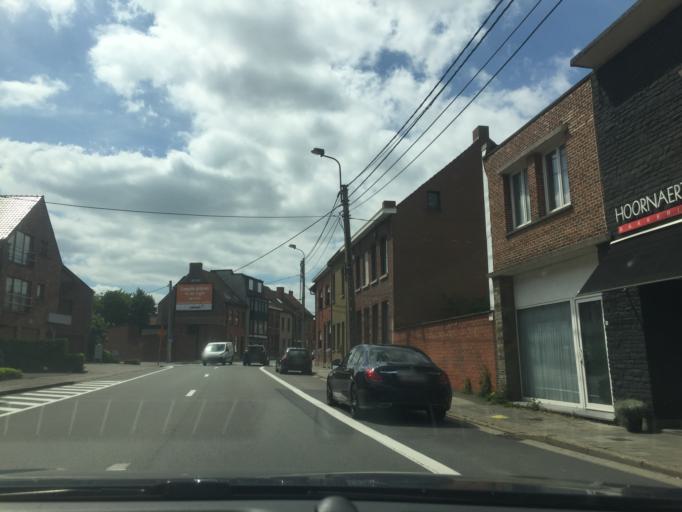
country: BE
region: Flanders
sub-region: Provincie West-Vlaanderen
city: Zwevegem
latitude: 50.8129
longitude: 3.3296
